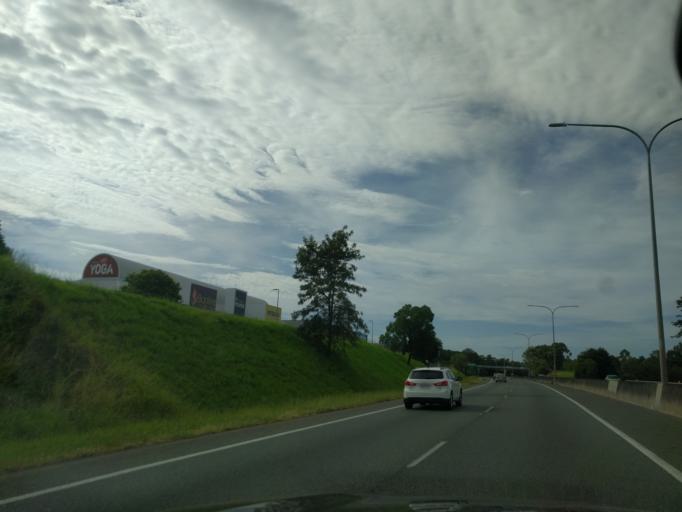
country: AU
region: Queensland
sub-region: Brisbane
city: Seventeen Mile Rocks
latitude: -27.5328
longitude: 152.9464
